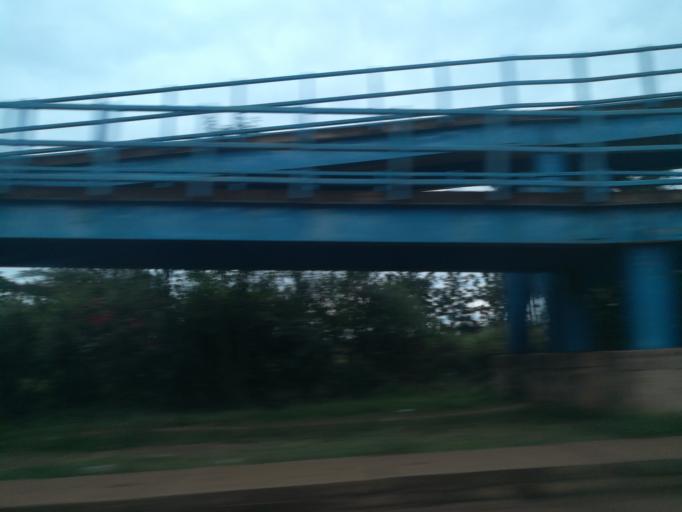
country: KE
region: Nairobi Area
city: Thika
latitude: -1.0759
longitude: 37.0464
